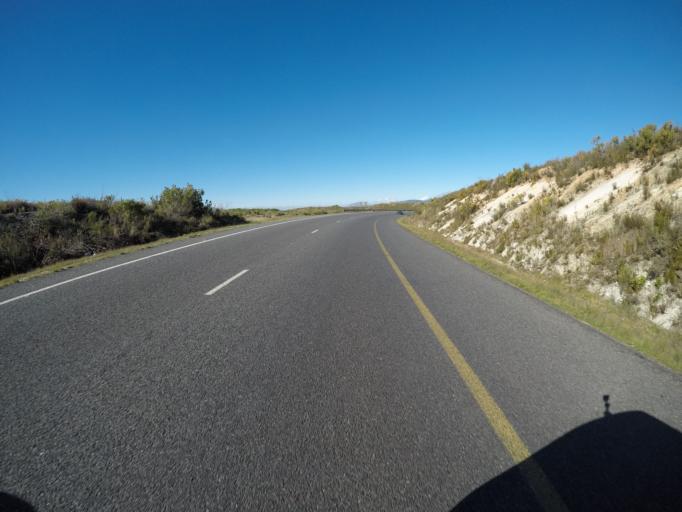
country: ZA
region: Western Cape
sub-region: Overberg District Municipality
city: Grabouw
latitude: -34.2168
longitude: 19.1718
